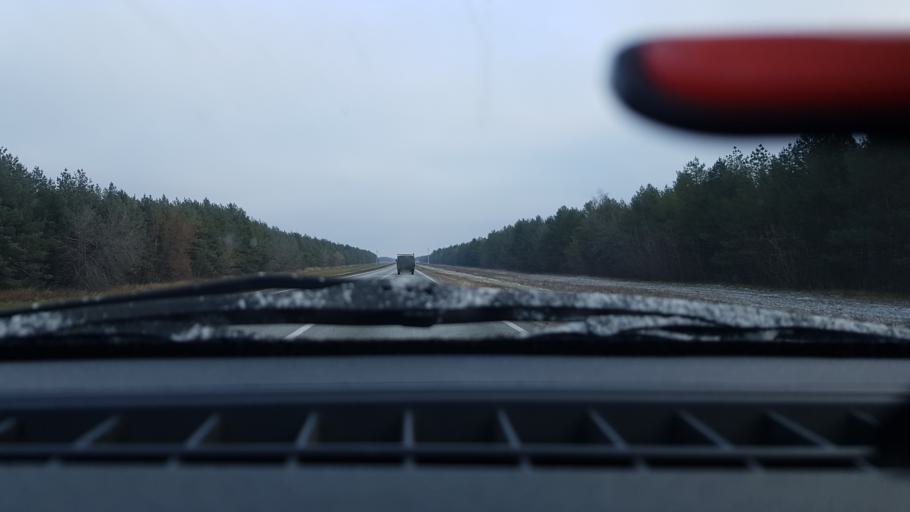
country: RU
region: Tatarstan
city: Kuybyshevskiy Zaton
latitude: 54.9465
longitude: 49.4525
